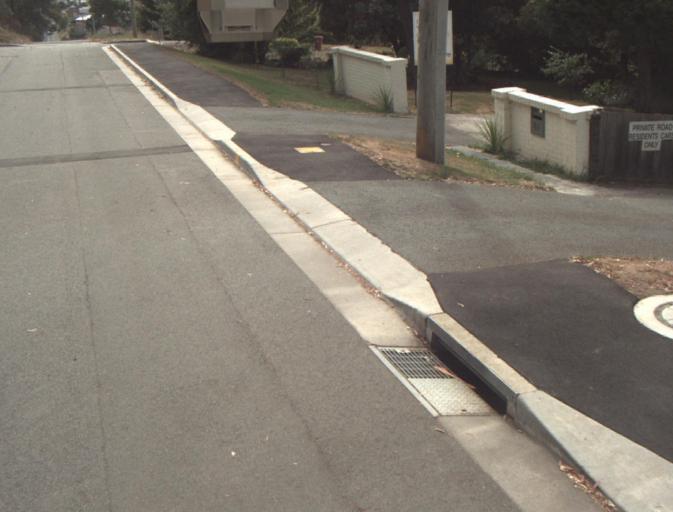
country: AU
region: Tasmania
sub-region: Launceston
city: Summerhill
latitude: -41.4623
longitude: 147.1404
